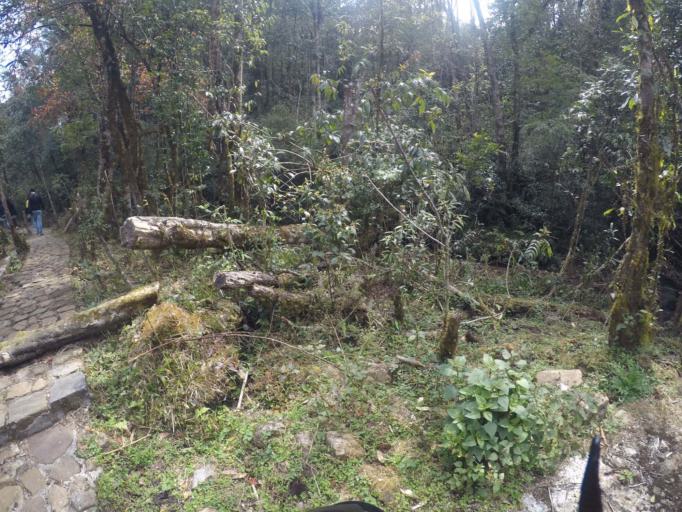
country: VN
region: Lao Cai
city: Sa Pa
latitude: 22.3488
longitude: 103.7707
